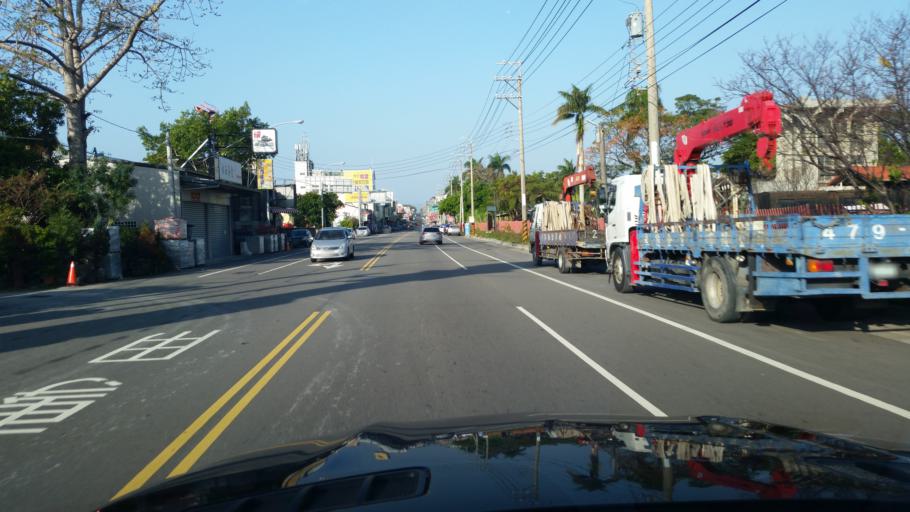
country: TW
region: Taiwan
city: Fengyuan
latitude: 24.3133
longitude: 120.6960
